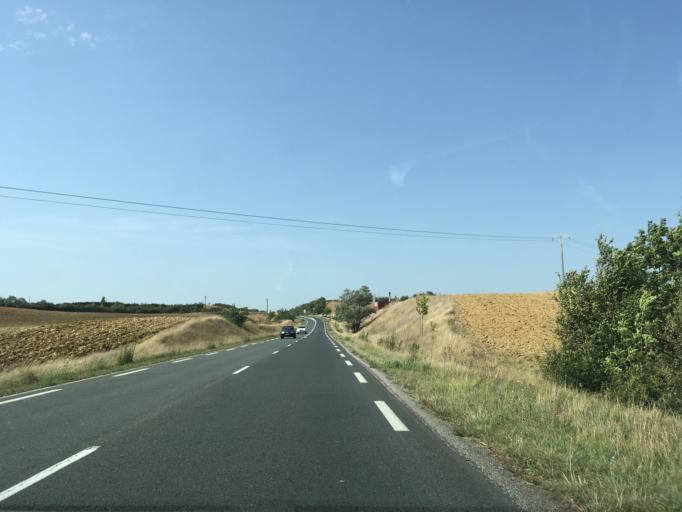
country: FR
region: Midi-Pyrenees
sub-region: Departement du Tarn
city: Lagarrigue
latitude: 43.5768
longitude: 2.2630
